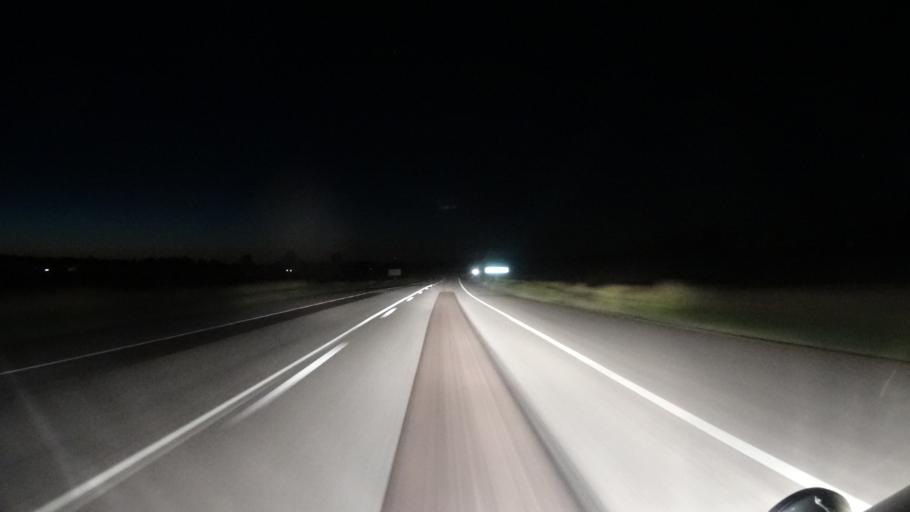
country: SE
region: OEstergoetland
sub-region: Odeshogs Kommun
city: OEdeshoeg
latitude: 58.2456
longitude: 14.7221
